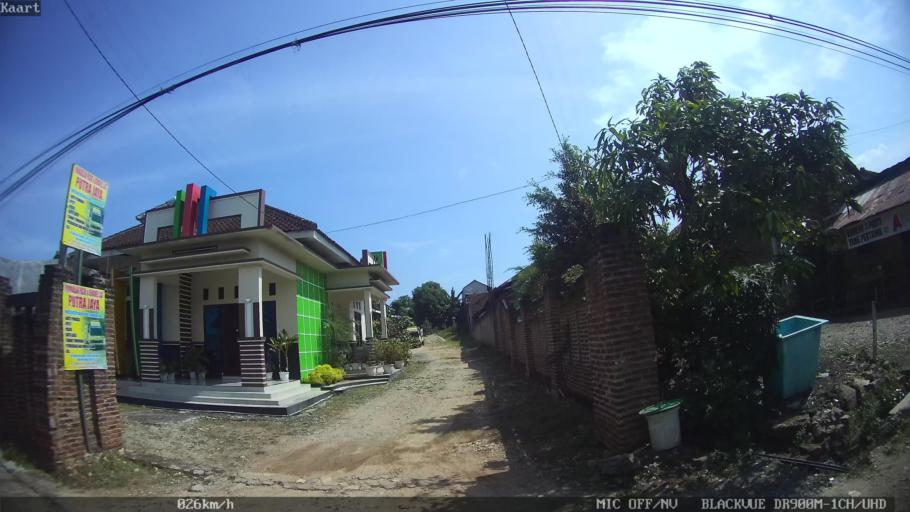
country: ID
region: Lampung
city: Kedaton
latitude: -5.3962
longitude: 105.2520
